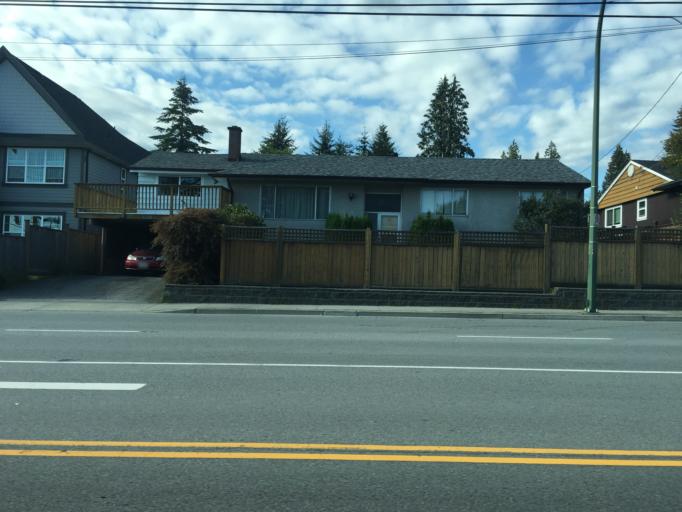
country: CA
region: British Columbia
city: Port Moody
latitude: 49.2490
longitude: -122.8519
